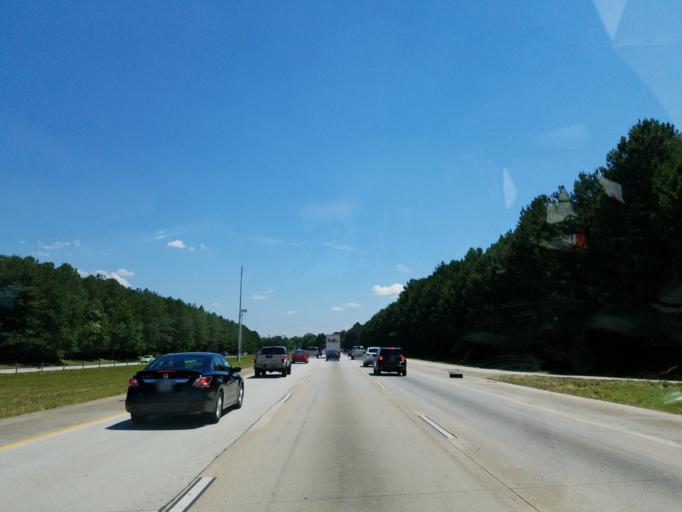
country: US
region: Georgia
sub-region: Clayton County
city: Lake City
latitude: 33.6087
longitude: -84.2960
